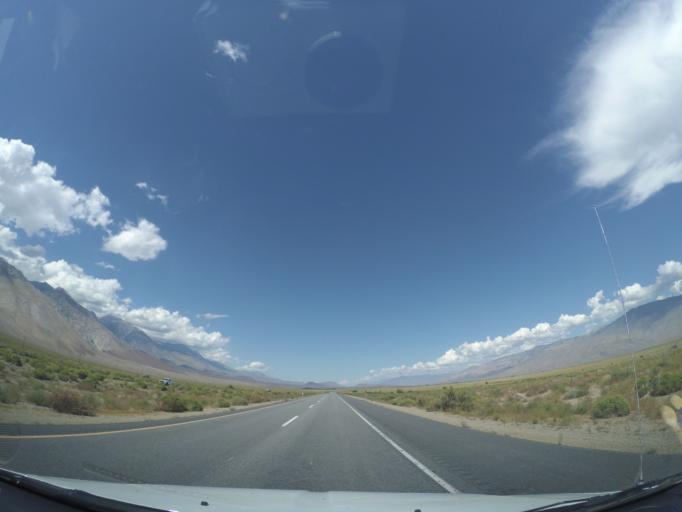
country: US
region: California
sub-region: Inyo County
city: Big Pine
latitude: 36.8823
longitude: -118.2398
